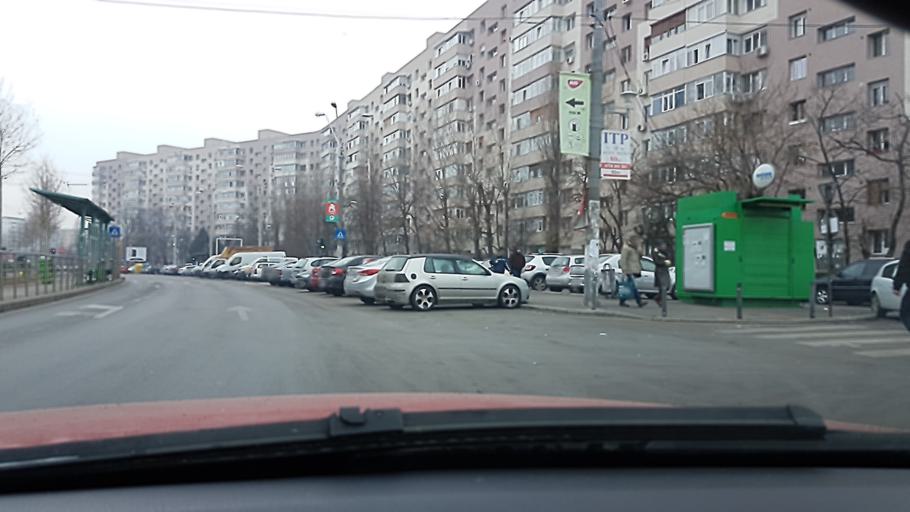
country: RO
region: Ilfov
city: Dobroesti
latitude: 44.4170
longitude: 26.1761
